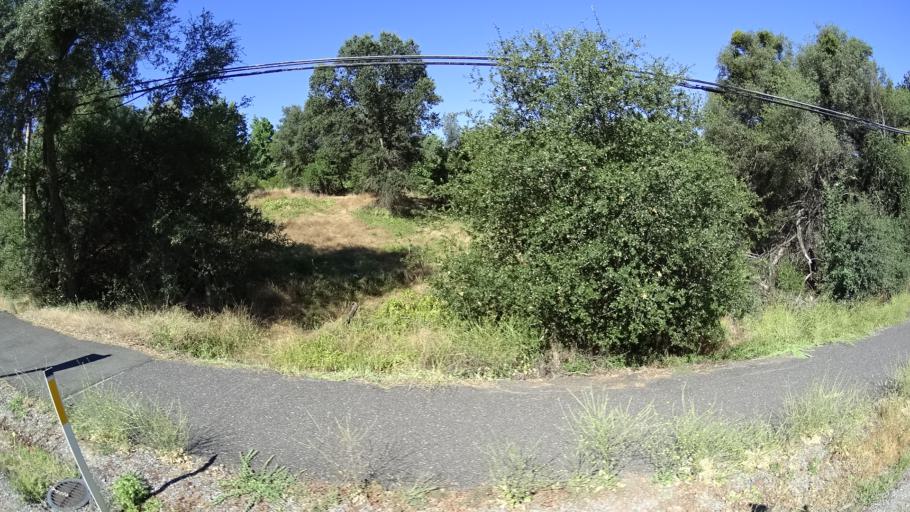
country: US
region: California
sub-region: Calaveras County
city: San Andreas
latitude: 38.2011
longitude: -120.6780
